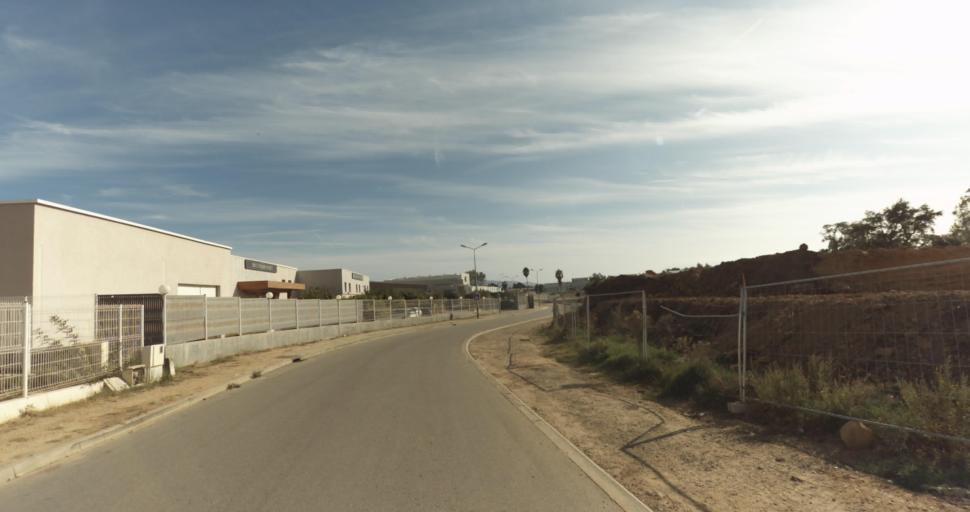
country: FR
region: Corsica
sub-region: Departement de la Corse-du-Sud
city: Afa
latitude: 41.9323
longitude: 8.7903
